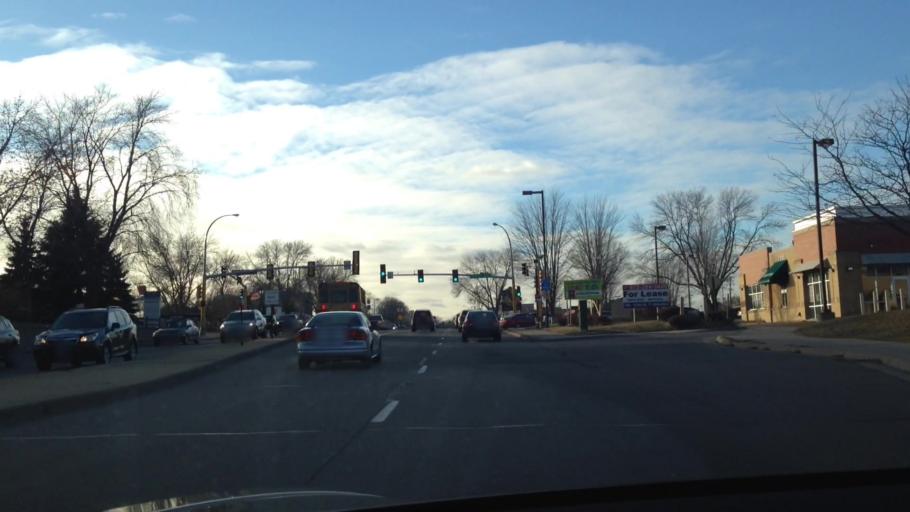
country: US
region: Minnesota
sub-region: Hennepin County
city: New Hope
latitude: 45.0329
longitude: -93.3755
